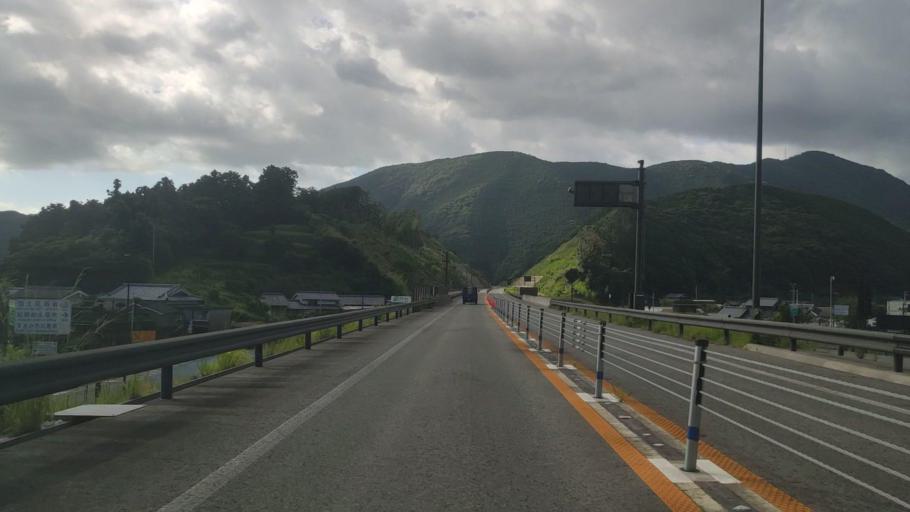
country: JP
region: Wakayama
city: Tanabe
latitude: 33.5553
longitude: 135.5099
